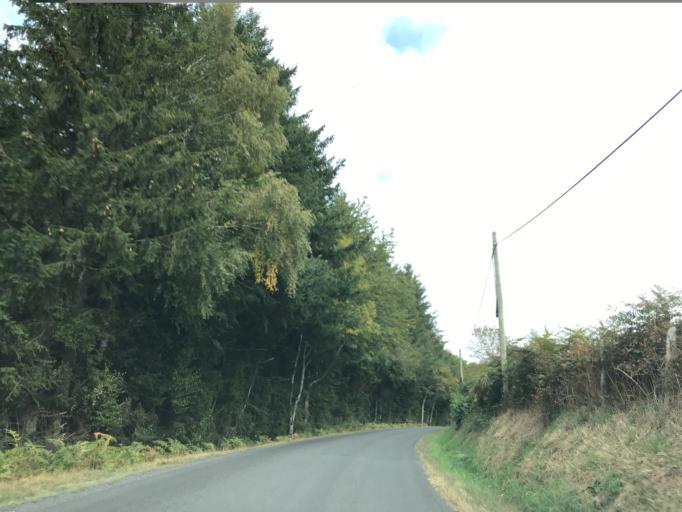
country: FR
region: Auvergne
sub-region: Departement du Puy-de-Dome
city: Celles-sur-Durolle
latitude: 45.8307
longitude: 3.6324
